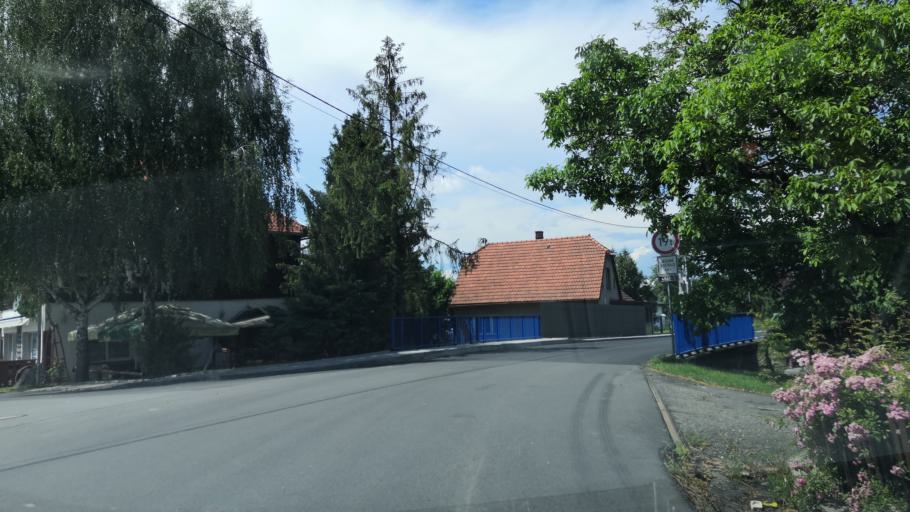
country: CZ
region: Zlin
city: Zasova
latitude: 49.4586
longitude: 18.0566
